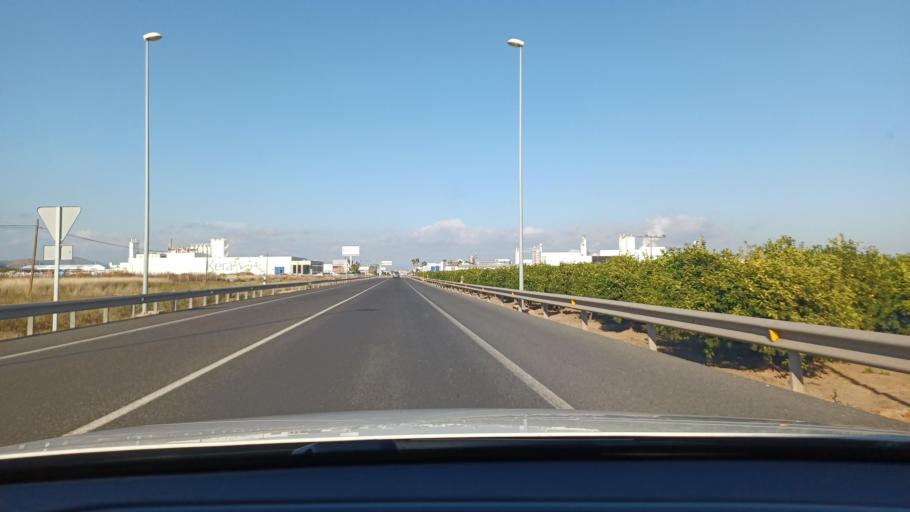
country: ES
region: Valencia
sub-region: Provincia de Castello
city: Moncofar
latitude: 39.8182
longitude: -0.1665
